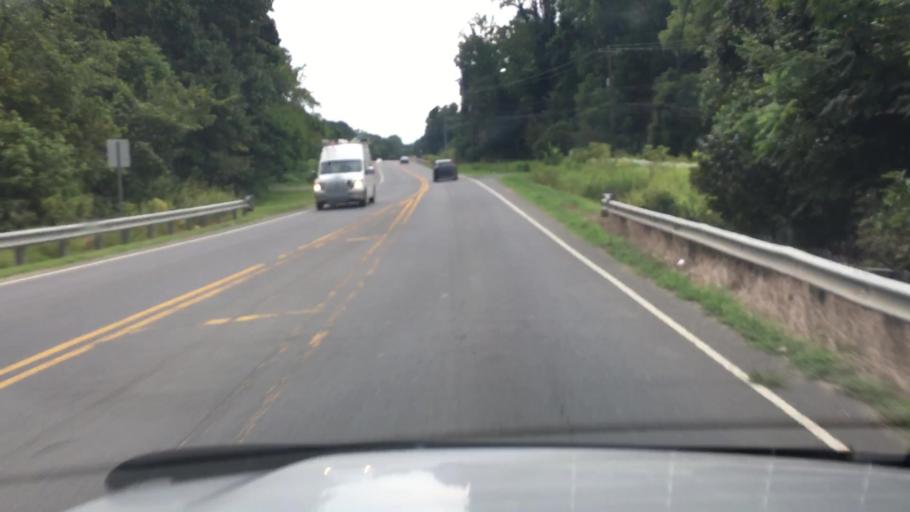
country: US
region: North Carolina
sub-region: Mecklenburg County
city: Huntersville
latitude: 35.3450
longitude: -80.8835
